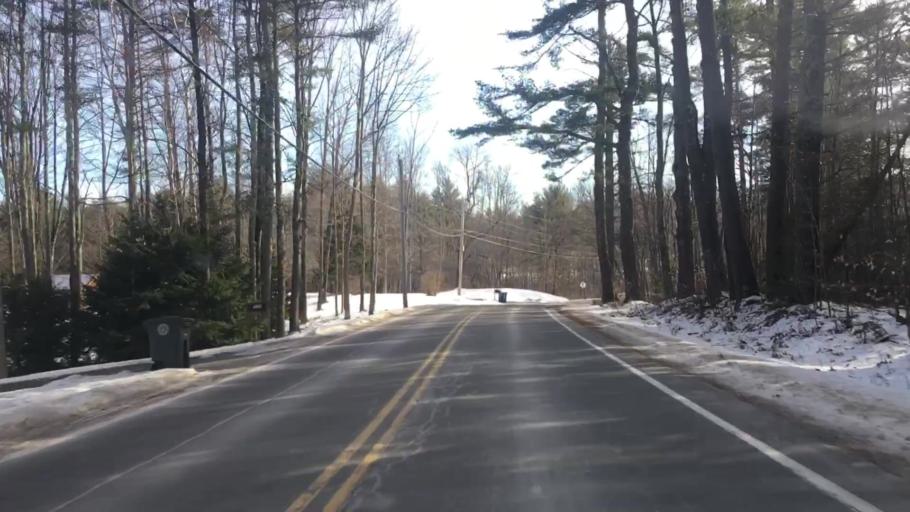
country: US
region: Maine
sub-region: Cumberland County
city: Westbrook
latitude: 43.7267
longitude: -70.3580
